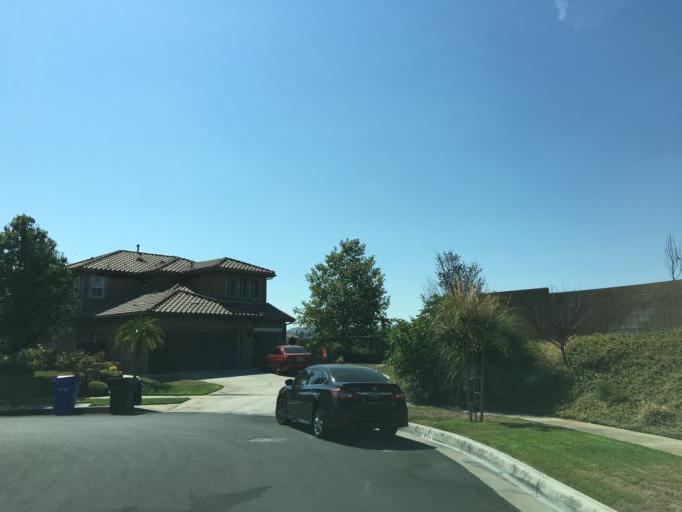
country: US
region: California
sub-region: Los Angeles County
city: Santa Clarita
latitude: 34.3868
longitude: -118.5733
